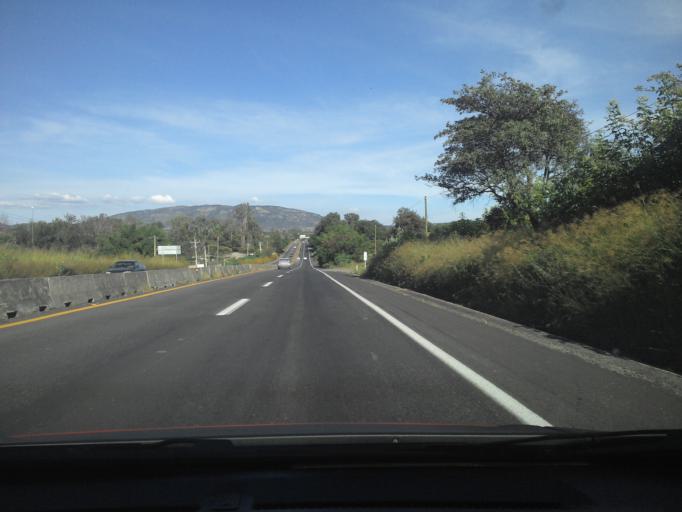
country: MX
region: Jalisco
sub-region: Tala
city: Los Ruisenores
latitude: 20.7170
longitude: -103.6392
